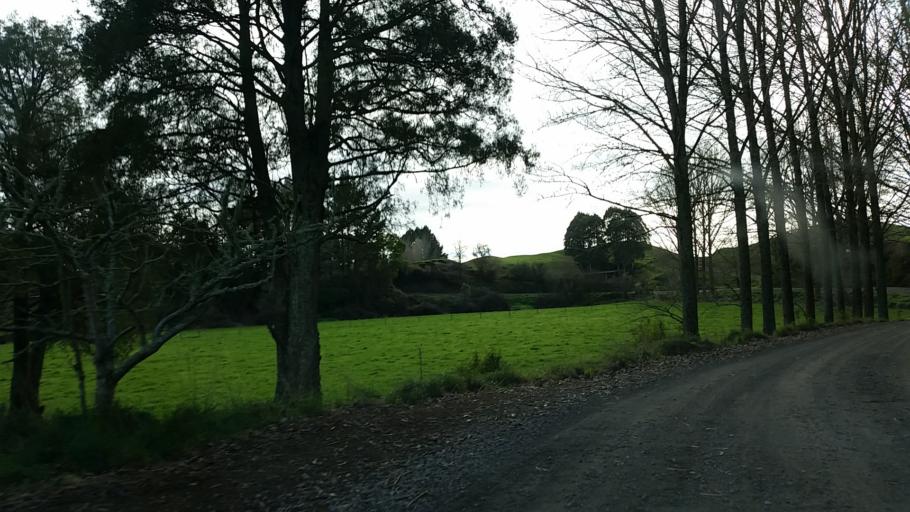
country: NZ
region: Taranaki
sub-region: South Taranaki District
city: Eltham
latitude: -39.2547
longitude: 174.5101
